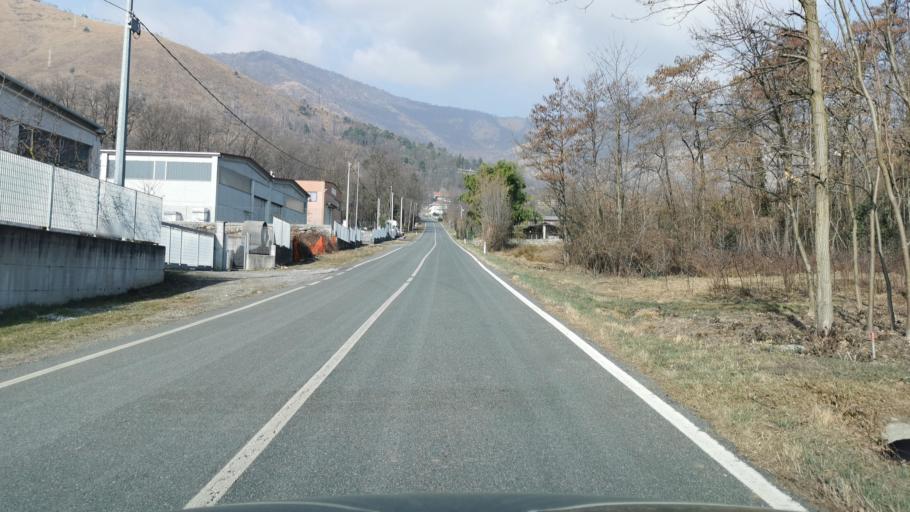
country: IT
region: Piedmont
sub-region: Provincia di Torino
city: Vallo Torinese
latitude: 45.2190
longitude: 7.4980
